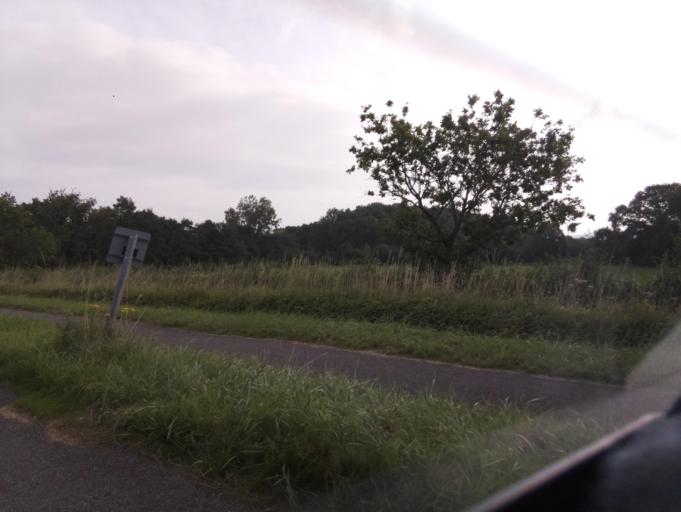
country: GB
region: England
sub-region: Bath and North East Somerset
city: Compton Martin
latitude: 51.3369
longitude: -2.6399
